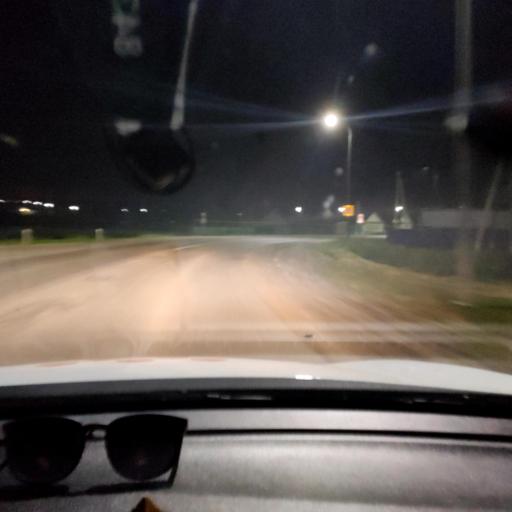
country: RU
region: Tatarstan
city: Rybnaya Sloboda
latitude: 55.4785
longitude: 50.1331
